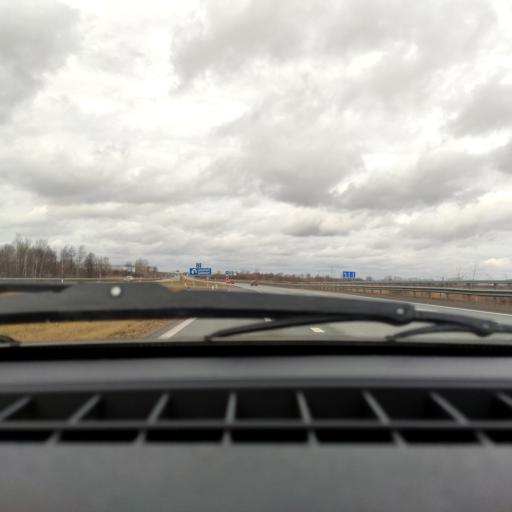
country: RU
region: Bashkortostan
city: Asanovo
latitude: 54.9659
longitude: 55.5825
